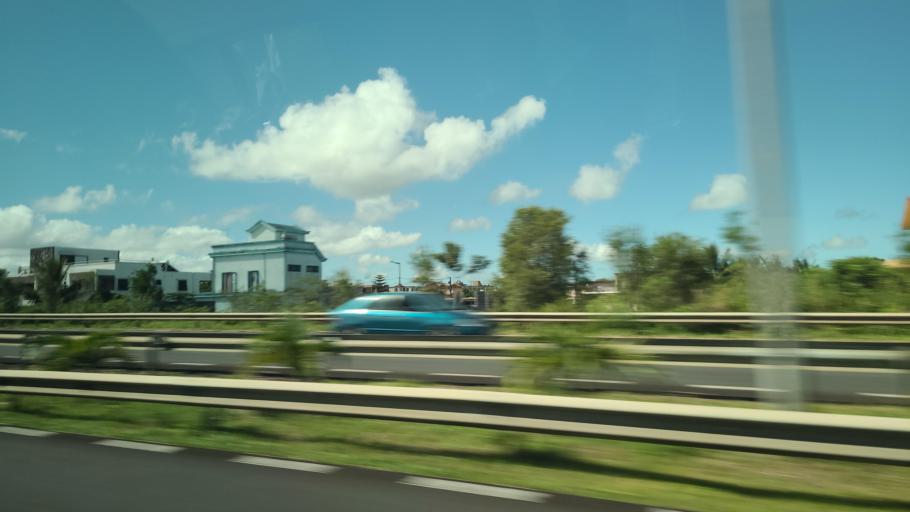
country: MU
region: Grand Port
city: Rose Belle
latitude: -20.4085
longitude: 57.5998
